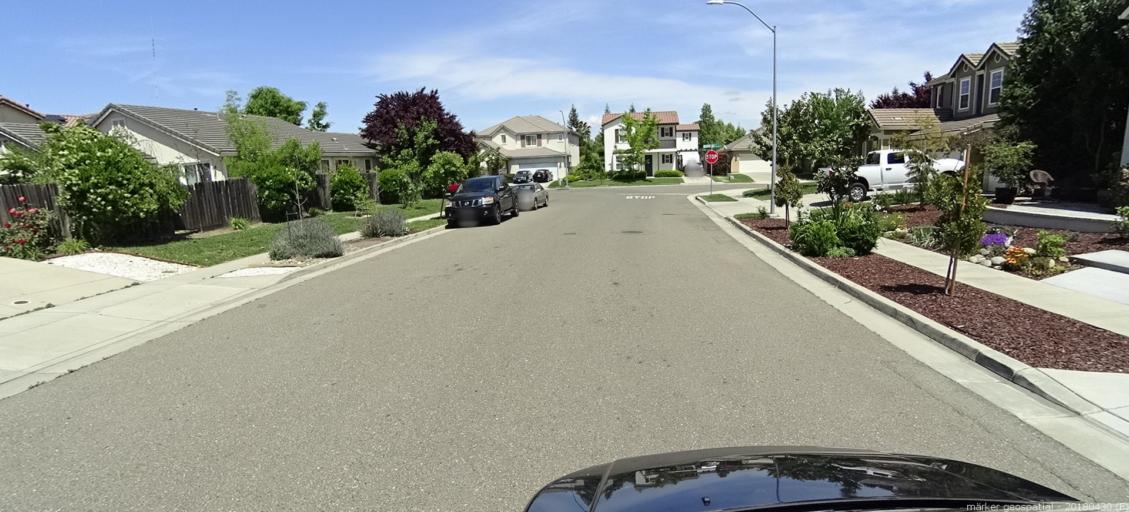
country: US
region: California
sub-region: Yolo County
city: West Sacramento
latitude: 38.5513
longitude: -121.5208
